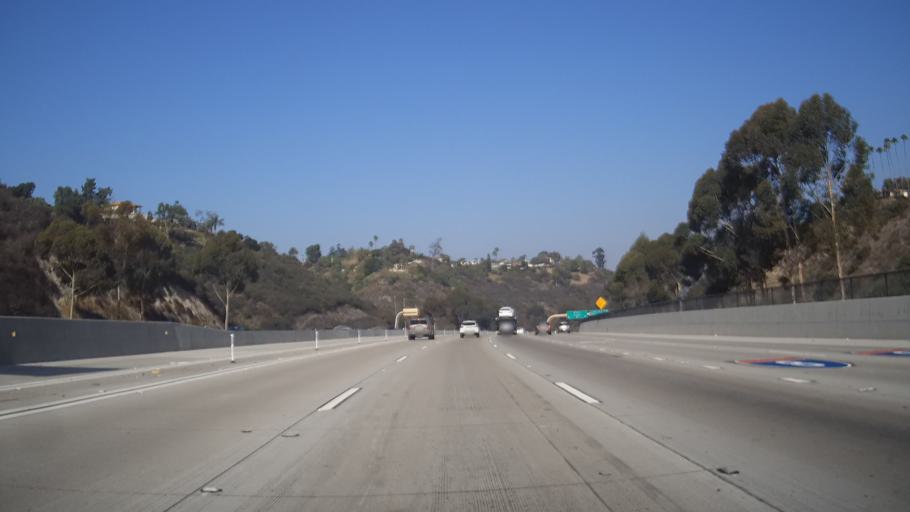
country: US
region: California
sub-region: San Diego County
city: San Diego
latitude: 32.7692
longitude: -117.1108
